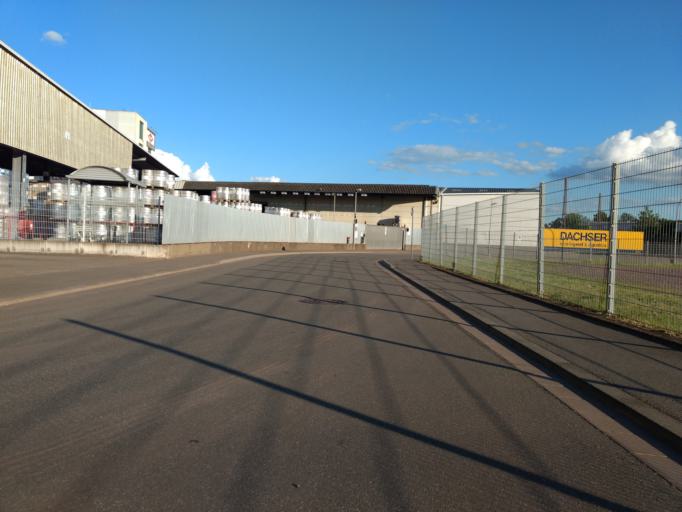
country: DE
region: Saarland
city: Saarlouis
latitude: 49.3273
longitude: 6.7595
